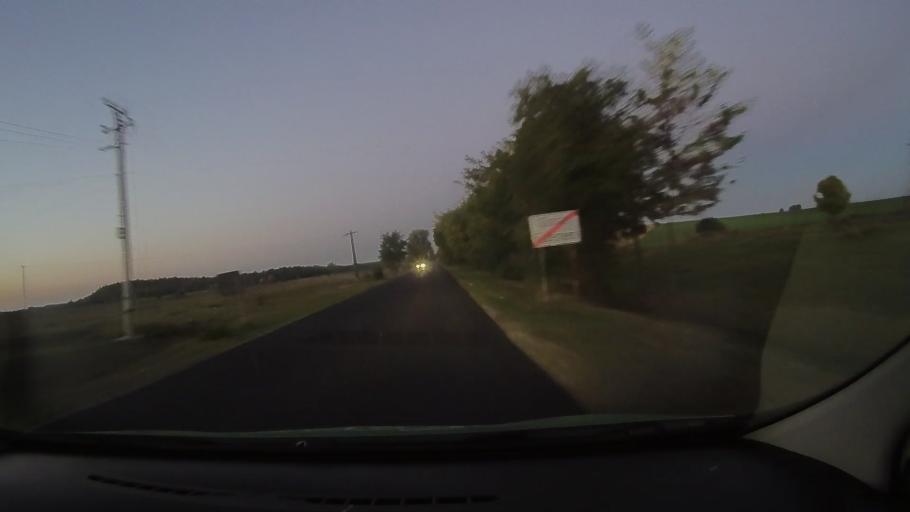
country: RO
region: Bihor
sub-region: Comuna Simian
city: Simian
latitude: 47.5038
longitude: 22.0927
